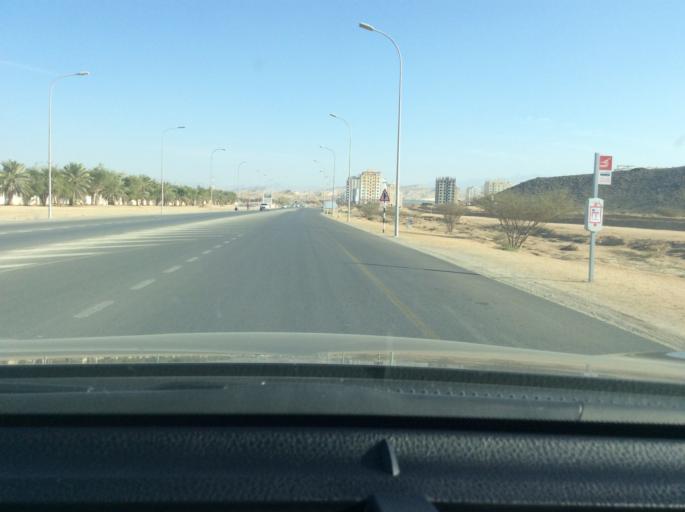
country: OM
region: Muhafazat Masqat
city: As Sib al Jadidah
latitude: 23.5803
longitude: 58.1752
